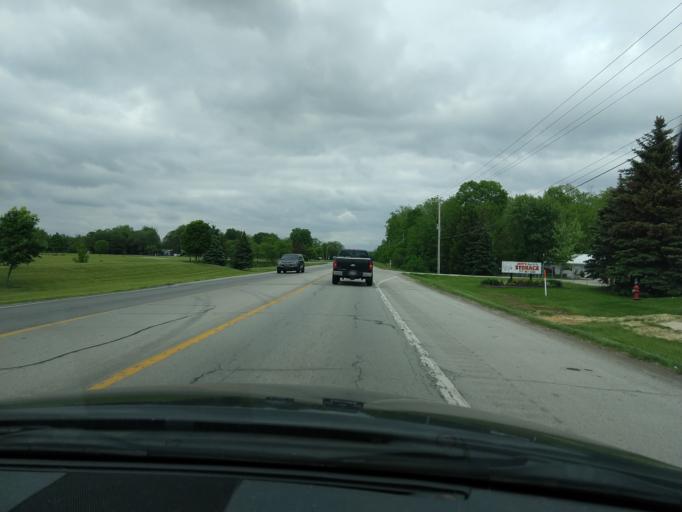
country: US
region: Indiana
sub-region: Hamilton County
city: Westfield
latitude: 40.0429
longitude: -86.1034
